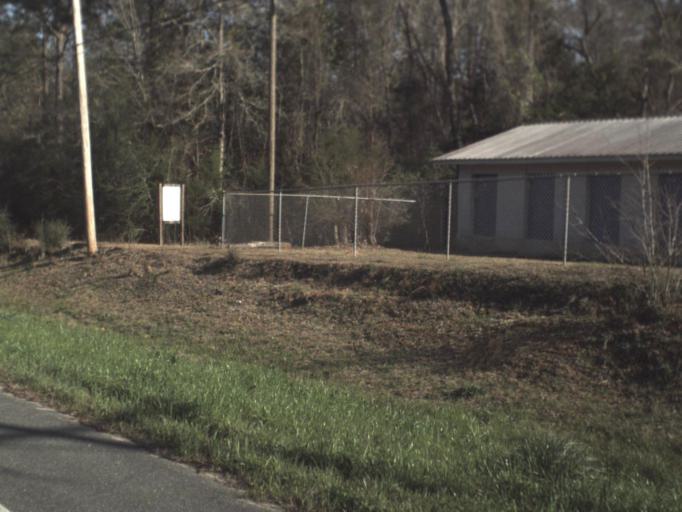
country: US
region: Florida
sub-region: Jackson County
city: Marianna
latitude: 30.7840
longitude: -85.2689
